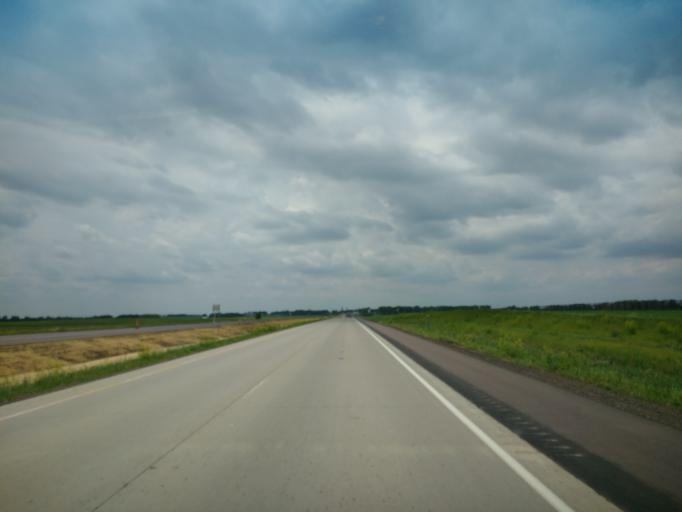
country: US
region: Minnesota
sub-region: Cottonwood County
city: Mountain Lake
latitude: 43.9185
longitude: -95.0006
